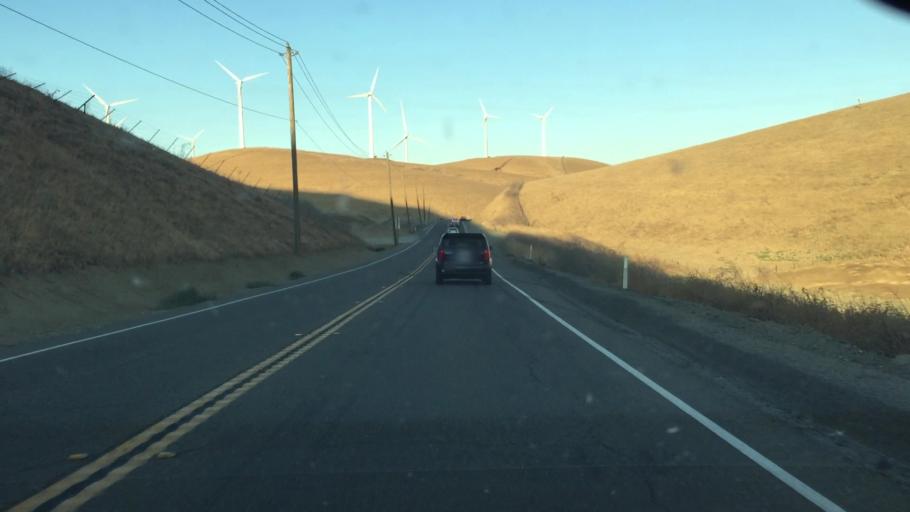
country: US
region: California
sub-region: San Joaquin County
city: Mountain House
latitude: 37.7451
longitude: -121.6334
